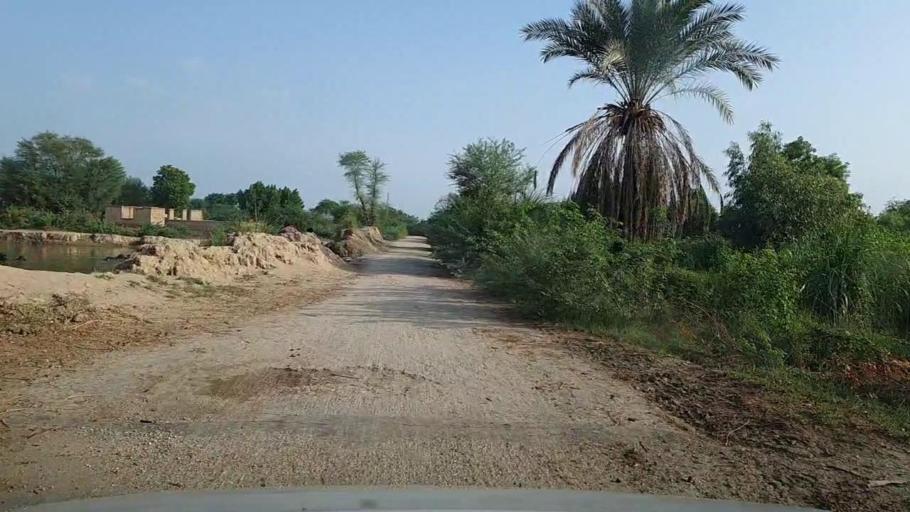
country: PK
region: Sindh
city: Pad Idan
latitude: 26.8091
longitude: 68.2349
